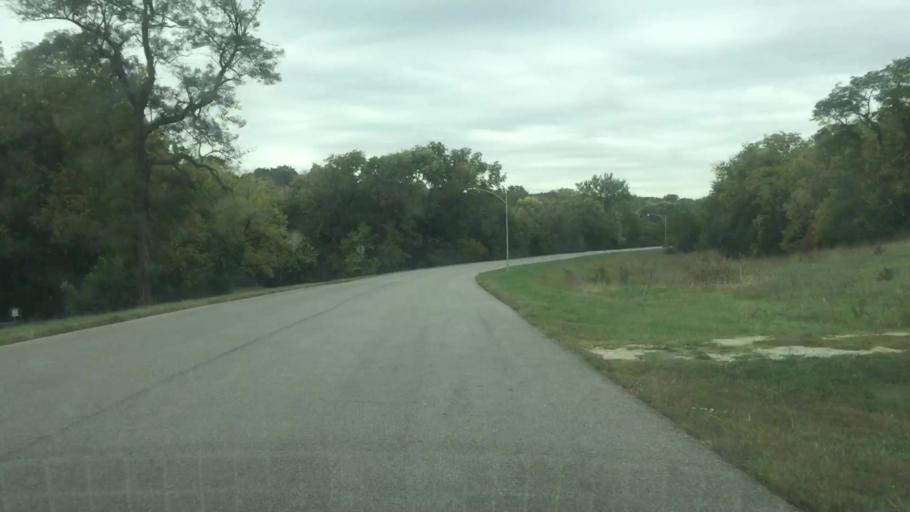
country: US
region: Kansas
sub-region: Johnson County
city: Lenexa
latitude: 38.9835
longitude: -94.7826
